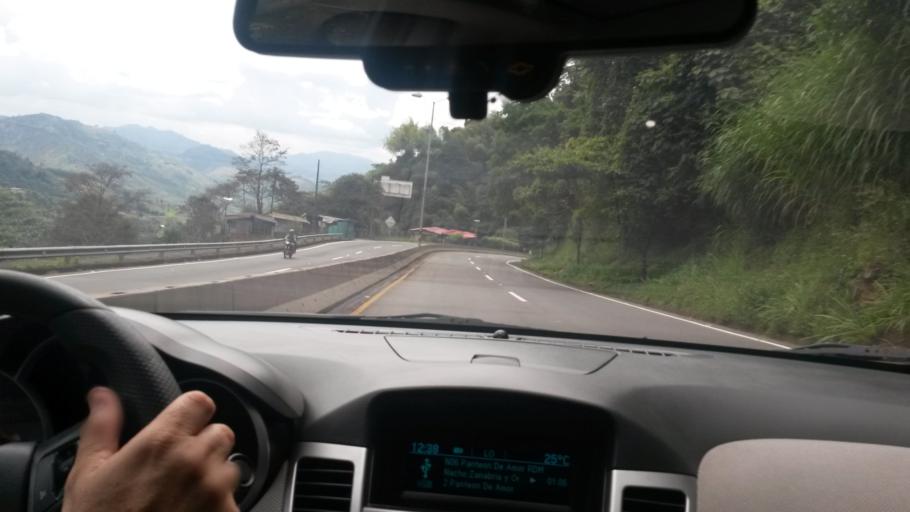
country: CO
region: Caldas
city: Manizales
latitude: 5.0558
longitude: -75.5705
